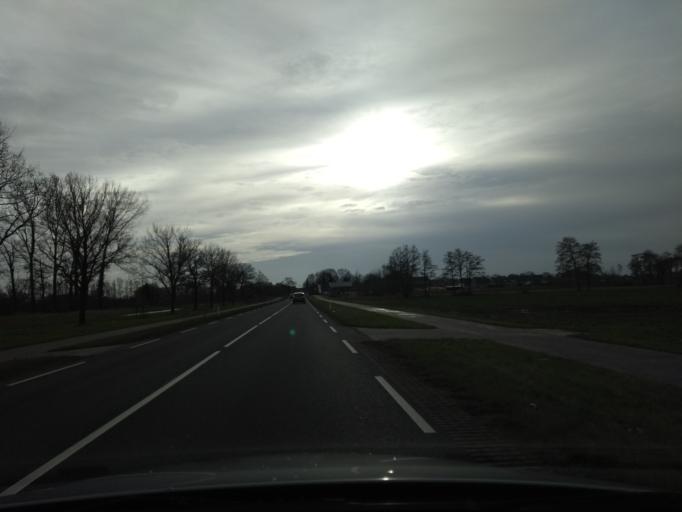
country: NL
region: Overijssel
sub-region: Gemeente Almelo
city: Almelo
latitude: 52.3172
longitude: 6.6548
